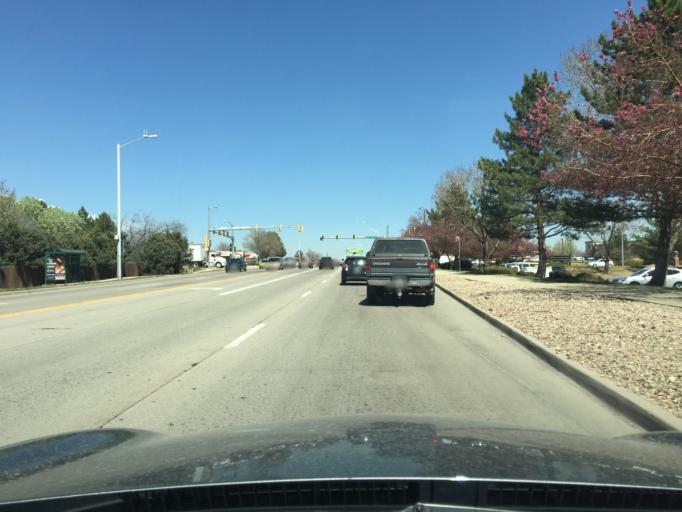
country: US
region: Colorado
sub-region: Boulder County
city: Longmont
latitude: 40.1877
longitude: -105.1308
